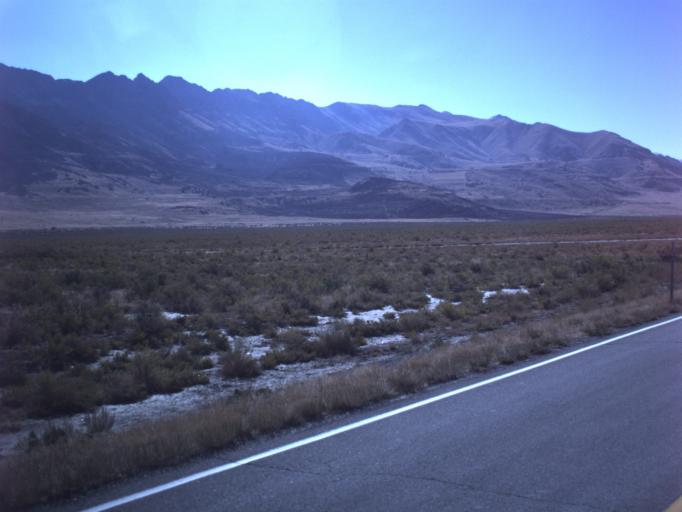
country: US
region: Utah
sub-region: Tooele County
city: Grantsville
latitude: 40.7347
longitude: -112.6563
